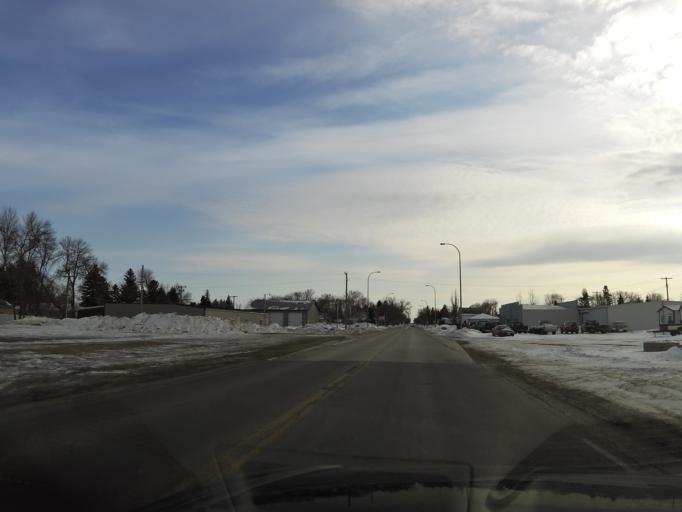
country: US
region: North Dakota
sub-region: Walsh County
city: Grafton
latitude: 48.5683
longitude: -97.1778
